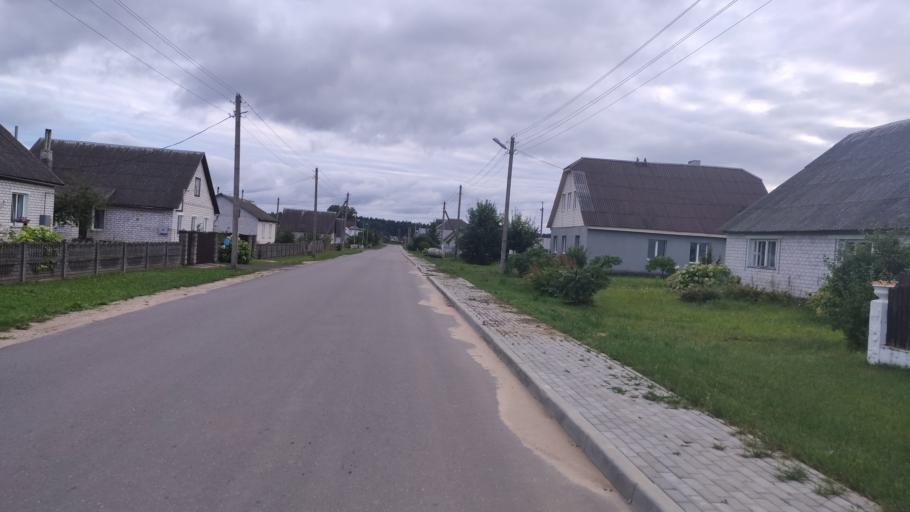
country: BY
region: Minsk
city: Narach
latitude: 54.9294
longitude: 26.6948
